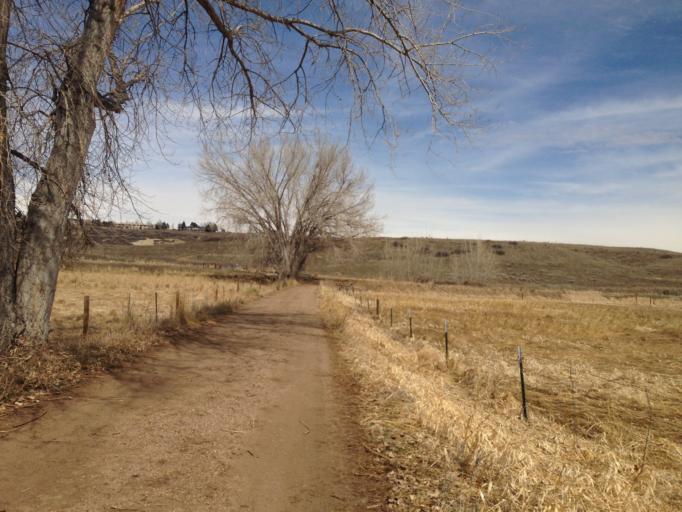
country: US
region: Colorado
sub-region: Boulder County
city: Gunbarrel
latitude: 40.0512
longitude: -105.1443
